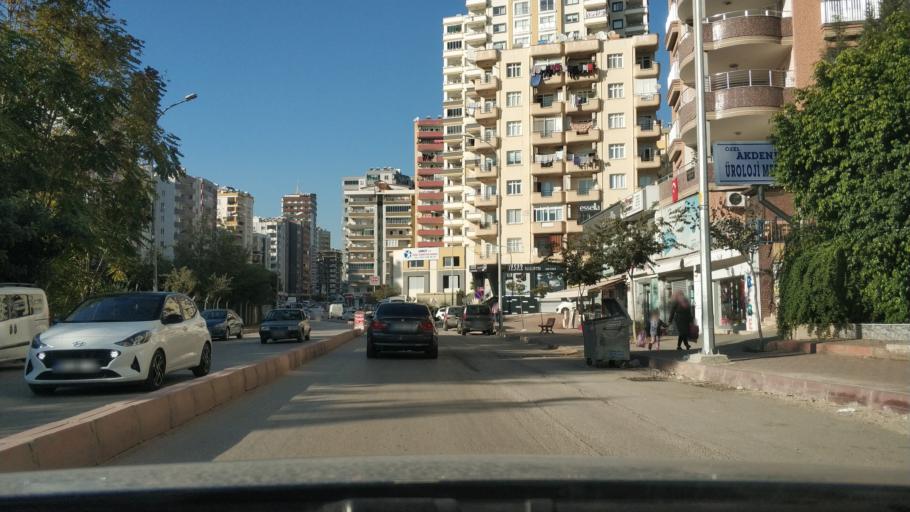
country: TR
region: Adana
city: Seyhan
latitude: 37.0512
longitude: 35.2788
